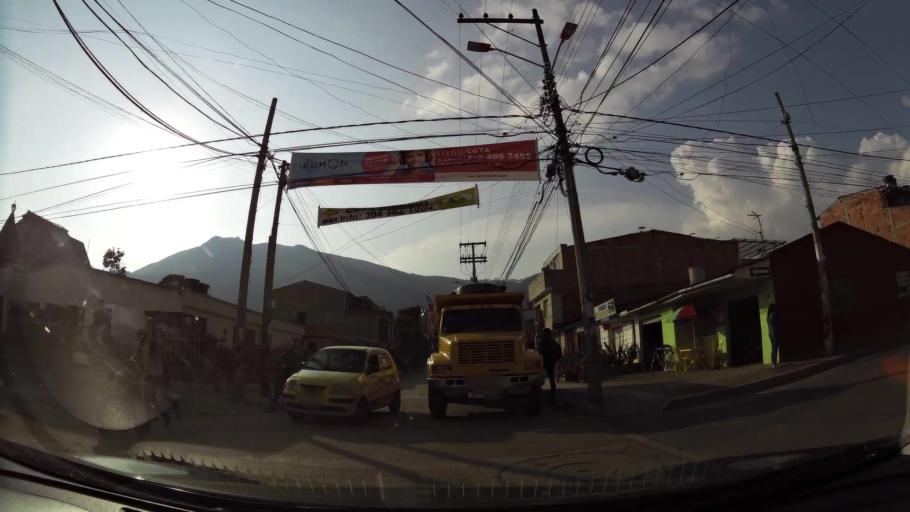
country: CO
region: Cundinamarca
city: Cota
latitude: 4.8122
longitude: -74.1008
